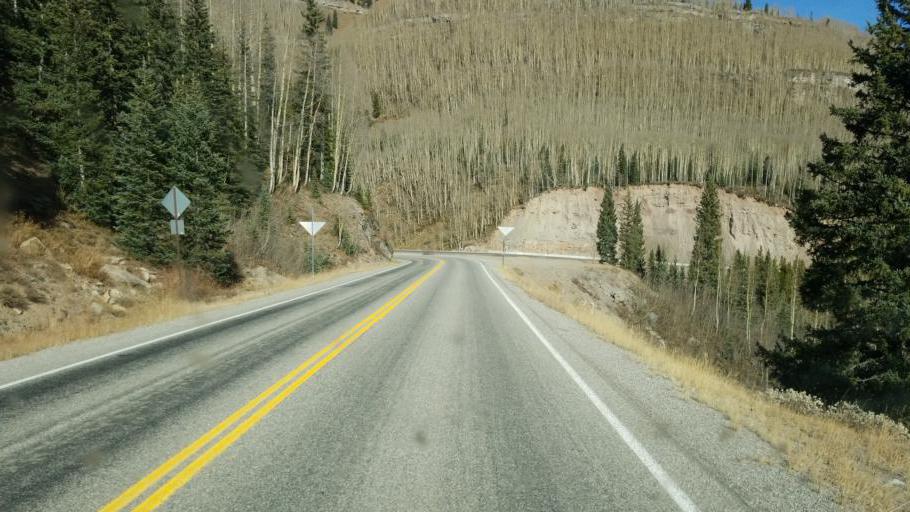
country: US
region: Colorado
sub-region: San Juan County
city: Silverton
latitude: 37.7164
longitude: -107.7552
